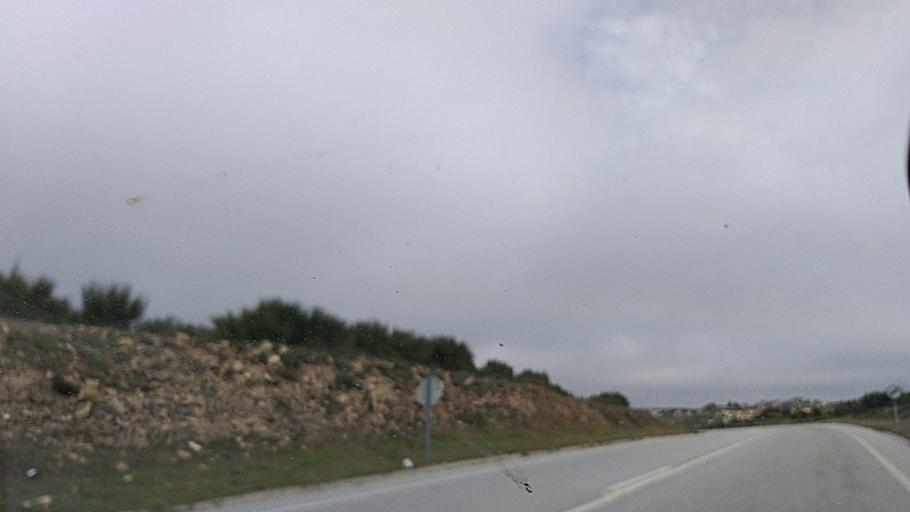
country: PT
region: Guarda
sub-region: Aguiar da Beira
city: Aguiar da Beira
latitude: 40.7618
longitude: -7.5021
